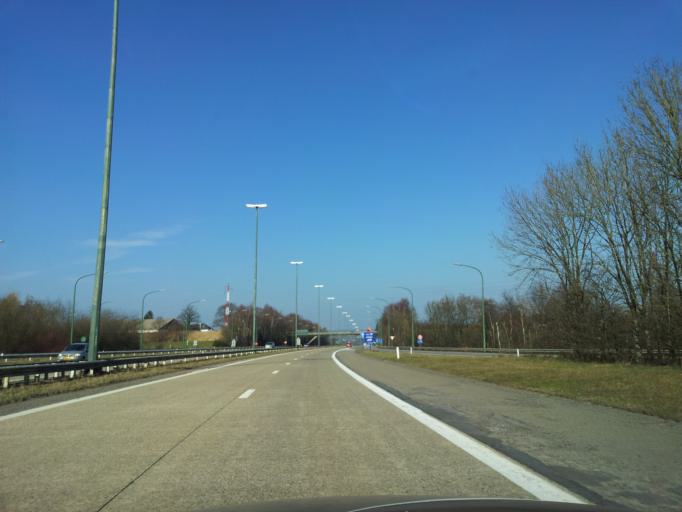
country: BE
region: Wallonia
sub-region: Province de Liege
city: Verviers
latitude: 50.5581
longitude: 5.8588
